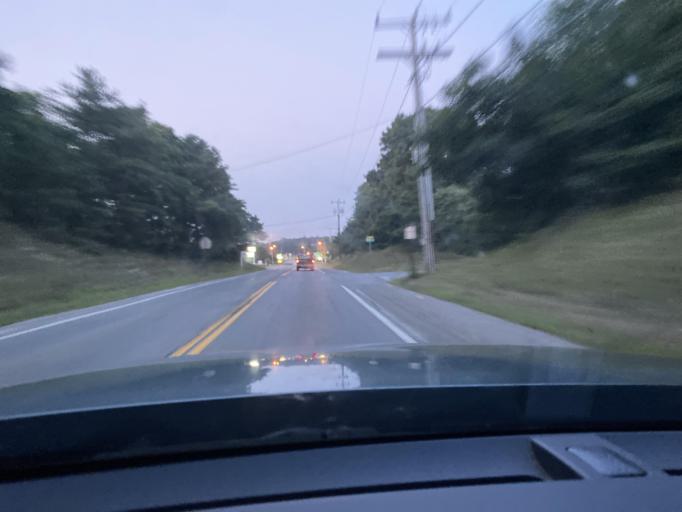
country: US
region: Massachusetts
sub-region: Barnstable County
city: Bourne
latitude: 41.7417
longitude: -70.5907
